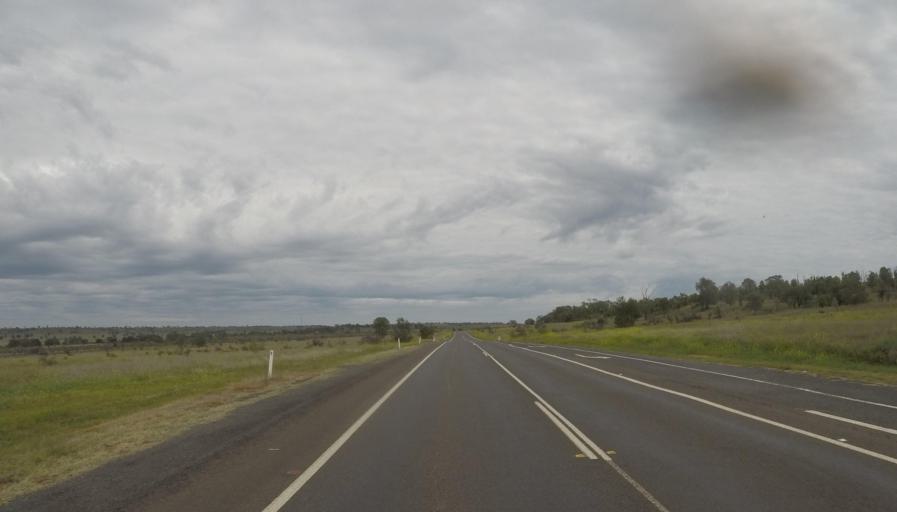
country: AU
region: Queensland
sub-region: Maranoa
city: Roma
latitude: -26.5366
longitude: 148.1565
